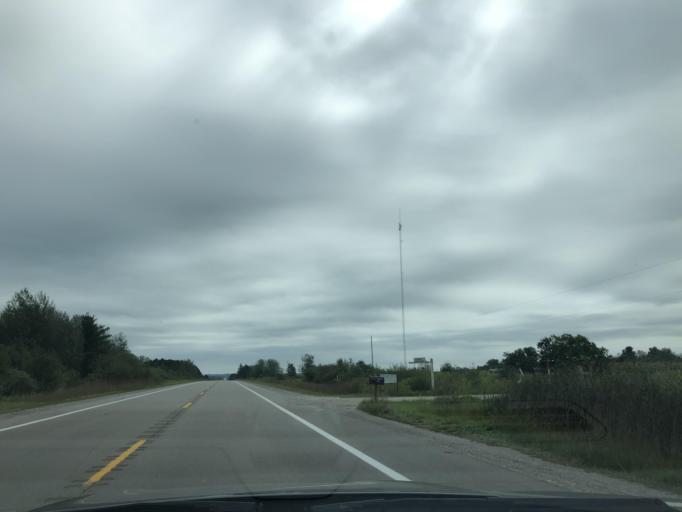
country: US
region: Michigan
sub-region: Clare County
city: Harrison
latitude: 44.0312
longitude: -84.9618
